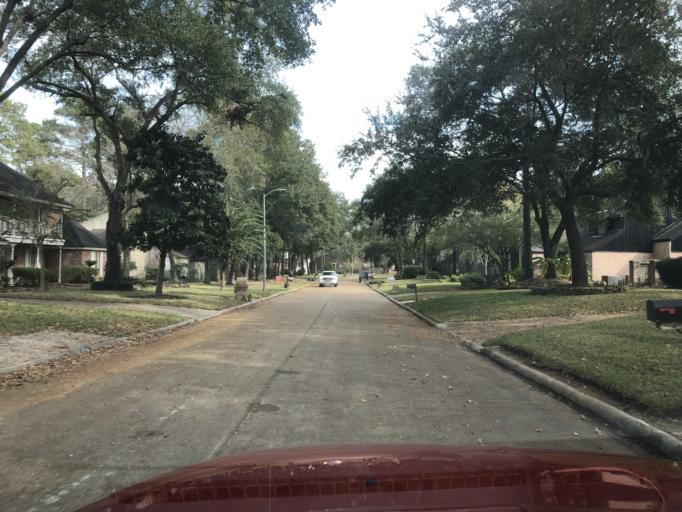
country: US
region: Texas
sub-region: Harris County
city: Spring
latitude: 30.0199
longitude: -95.4657
